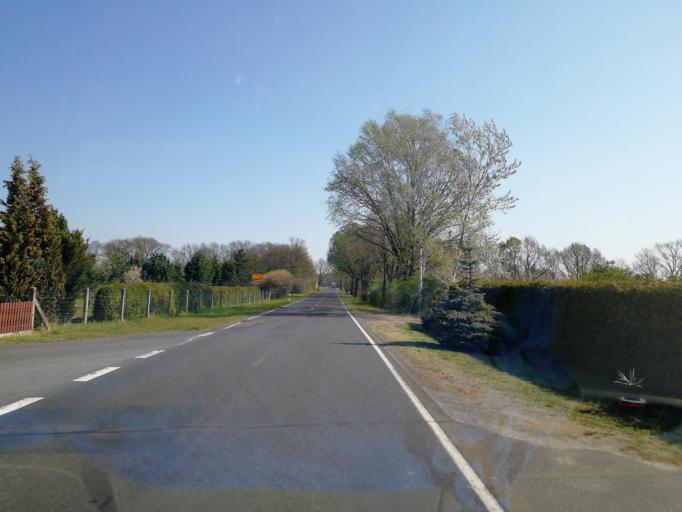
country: DE
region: Brandenburg
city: Calau
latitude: 51.7627
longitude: 13.8602
